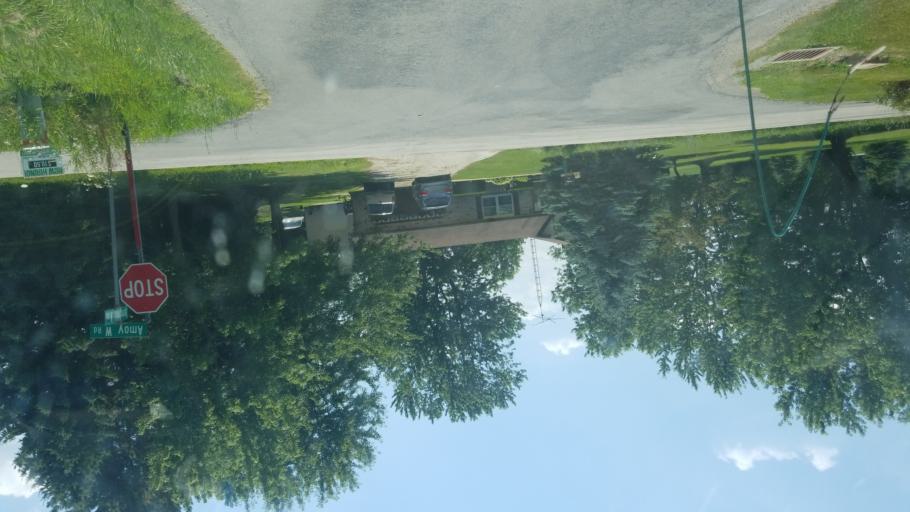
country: US
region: Ohio
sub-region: Richland County
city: Ontario
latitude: 40.8286
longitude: -82.5919
